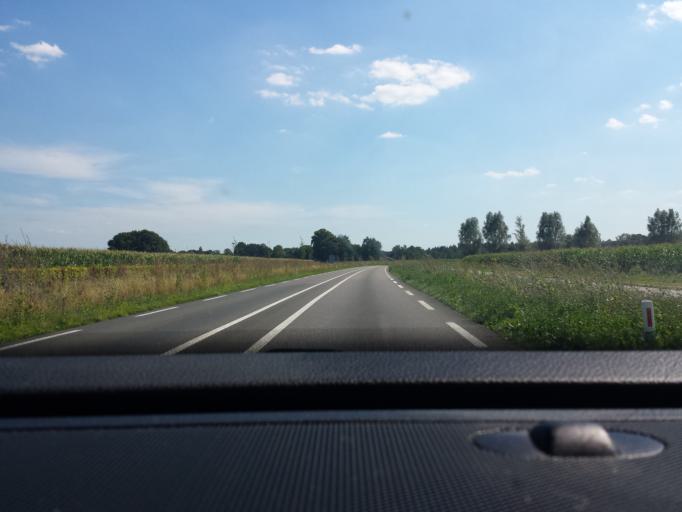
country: NL
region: Gelderland
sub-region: Gemeente Bronckhorst
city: Baak
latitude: 52.0119
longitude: 6.2288
